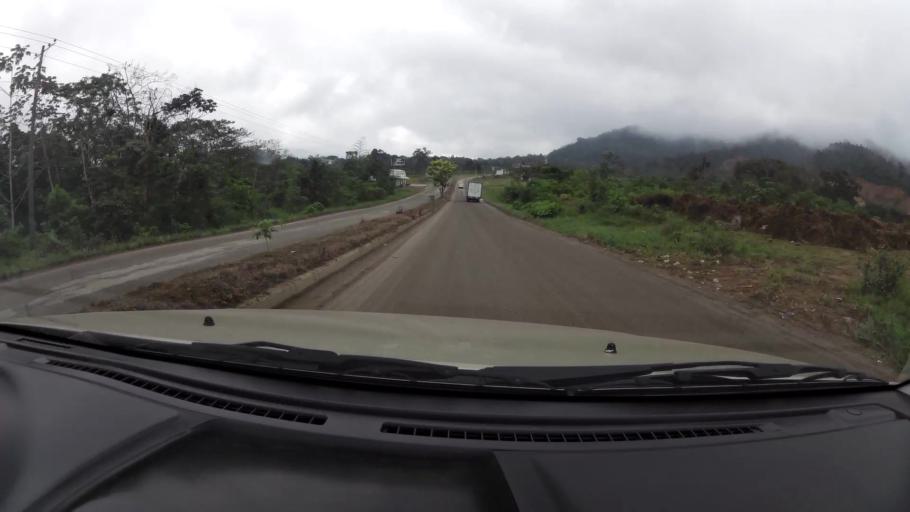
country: EC
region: El Oro
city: Pasaje
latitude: -3.3285
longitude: -79.7750
